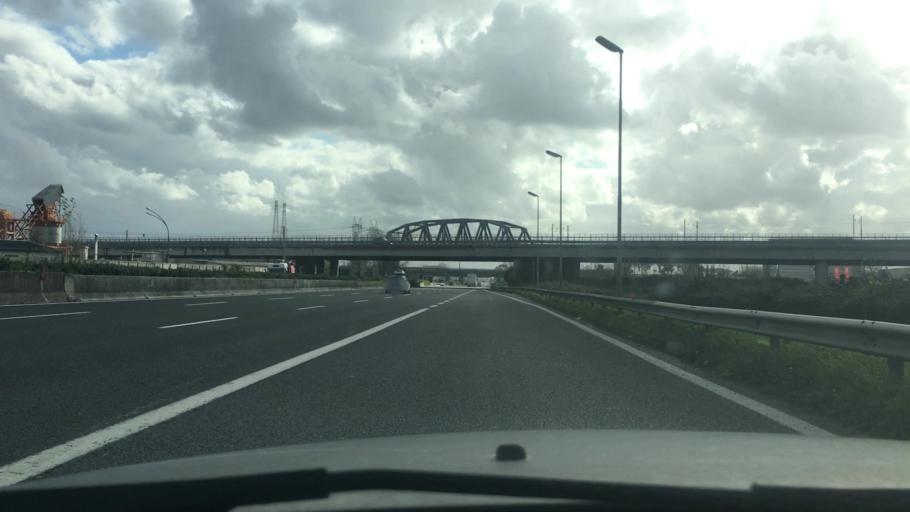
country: IT
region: Campania
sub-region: Provincia di Caserta
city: San Marco Evangelista
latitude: 41.0166
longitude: 14.3223
